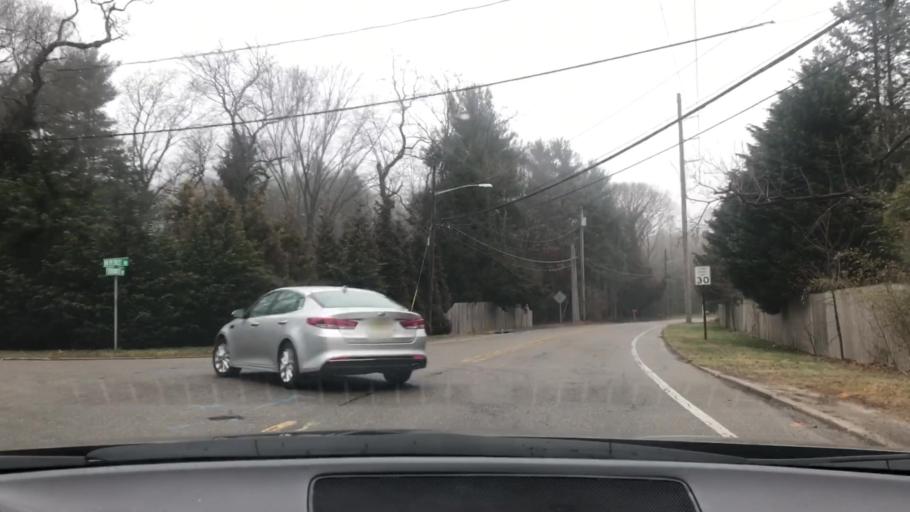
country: US
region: New York
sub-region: Suffolk County
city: South Huntington
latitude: 40.8232
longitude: -73.3716
